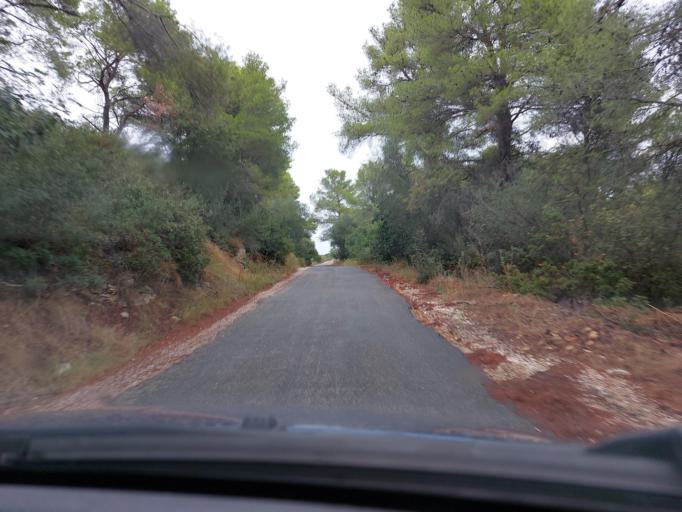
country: HR
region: Dubrovacko-Neretvanska
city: Smokvica
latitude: 42.7642
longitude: 16.9003
